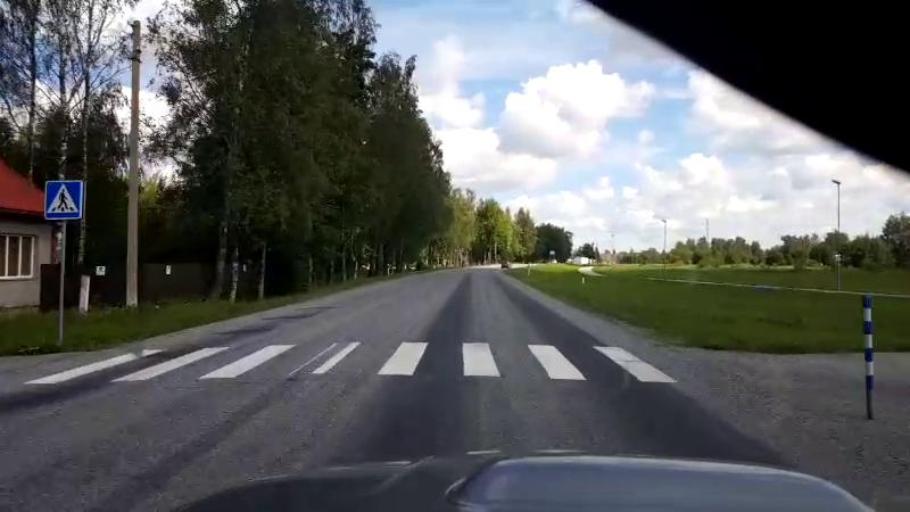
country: EE
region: Laeaene-Virumaa
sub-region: Tapa vald
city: Tapa
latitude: 59.2524
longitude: 25.9392
